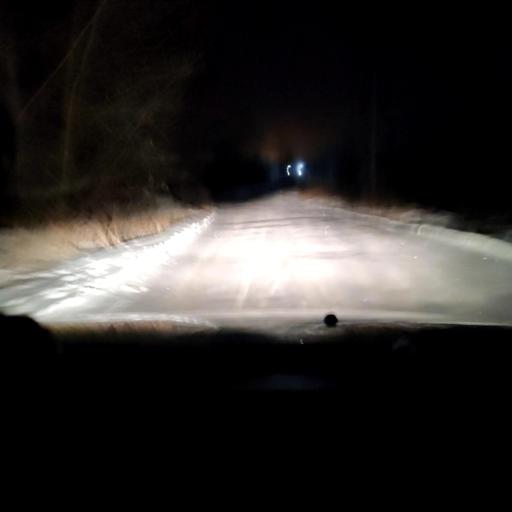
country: RU
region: Samara
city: Samara
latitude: 53.1504
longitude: 50.1897
